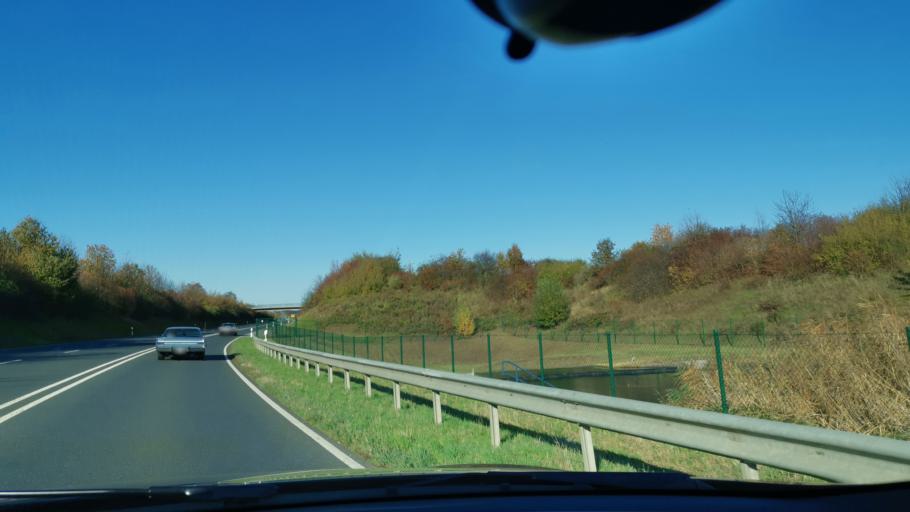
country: DE
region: North Rhine-Westphalia
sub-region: Regierungsbezirk Dusseldorf
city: Rommerskirchen
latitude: 51.0322
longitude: 6.6752
